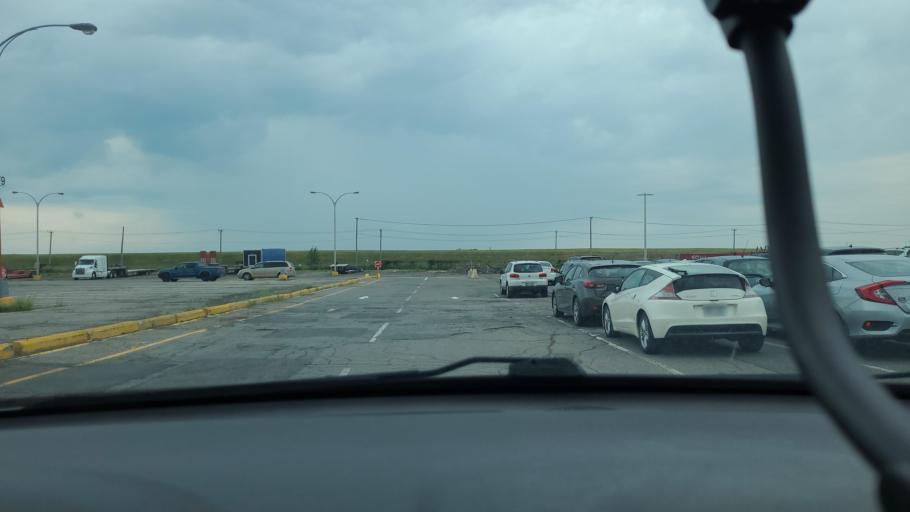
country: CA
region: Quebec
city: Dorval
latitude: 45.4739
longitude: -73.7365
